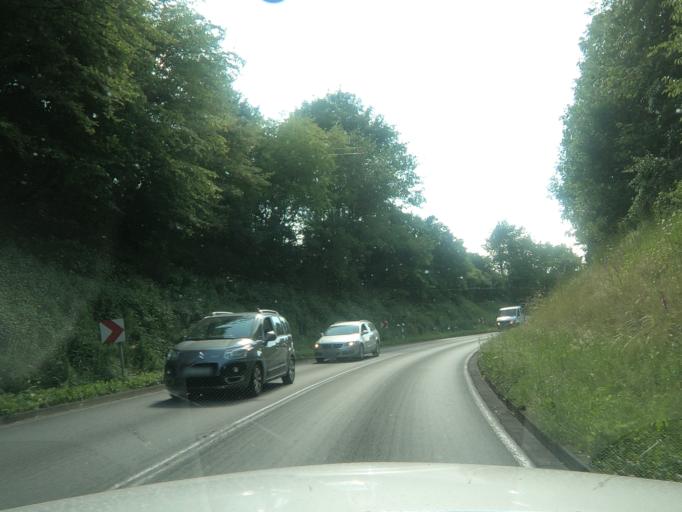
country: DE
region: North Rhine-Westphalia
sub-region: Regierungsbezirk Arnsberg
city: Finnentrop
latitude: 51.1336
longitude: 8.0097
